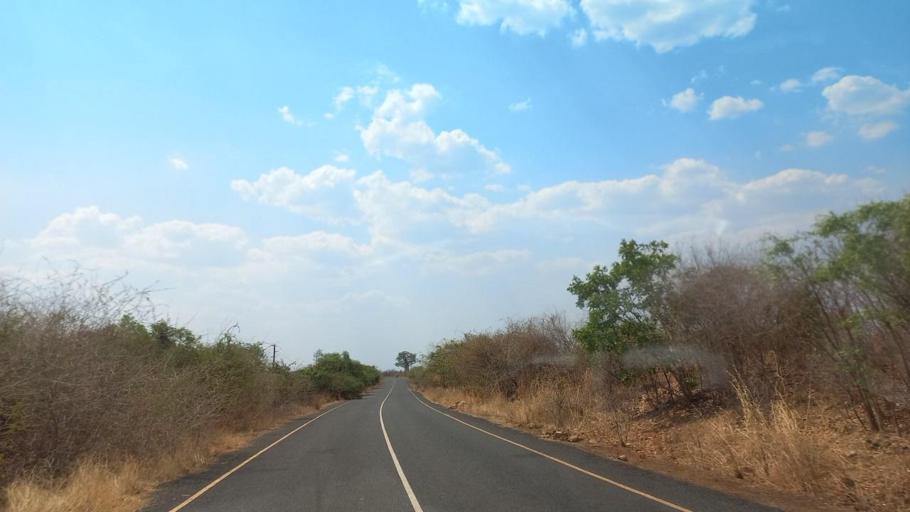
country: ZM
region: Lusaka
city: Luangwa
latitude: -15.3293
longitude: 30.3503
